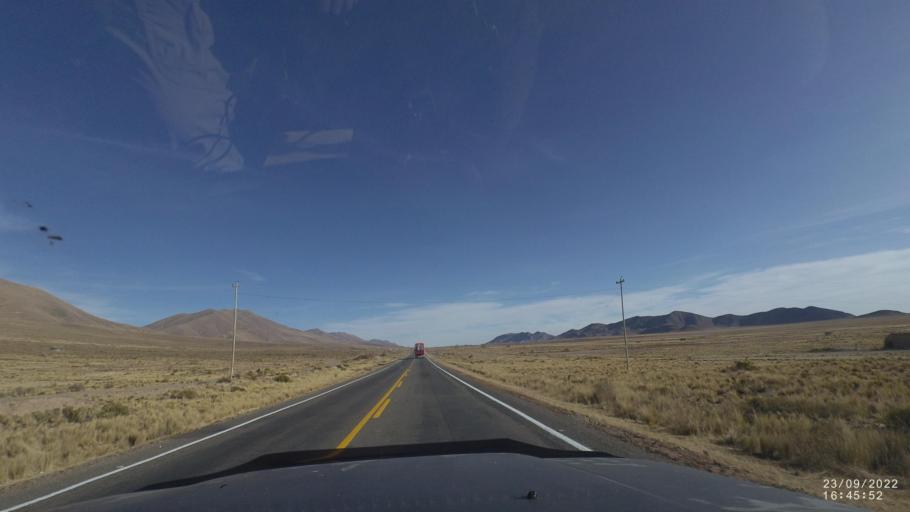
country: BO
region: Oruro
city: Poopo
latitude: -18.3474
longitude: -66.9851
